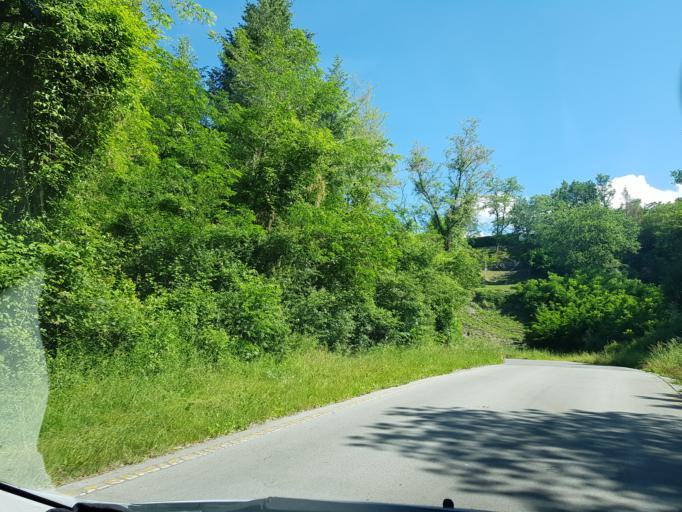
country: IT
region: Tuscany
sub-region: Provincia di Lucca
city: Camporgiano
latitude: 44.1648
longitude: 10.3388
